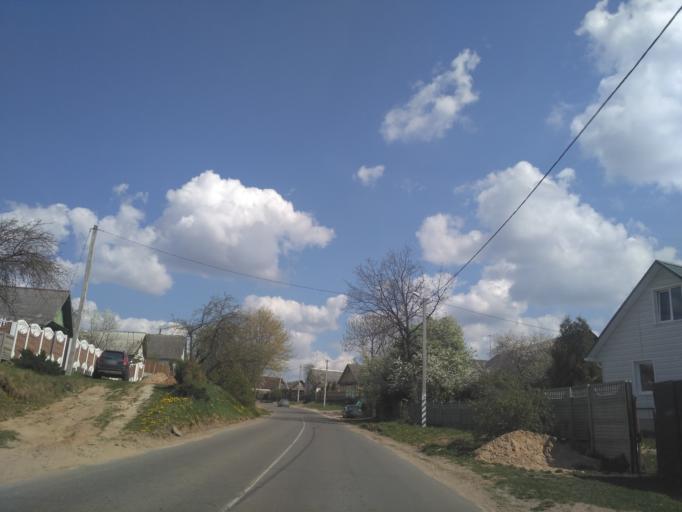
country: BY
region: Minsk
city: Radashkovichy
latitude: 54.1601
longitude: 27.2438
